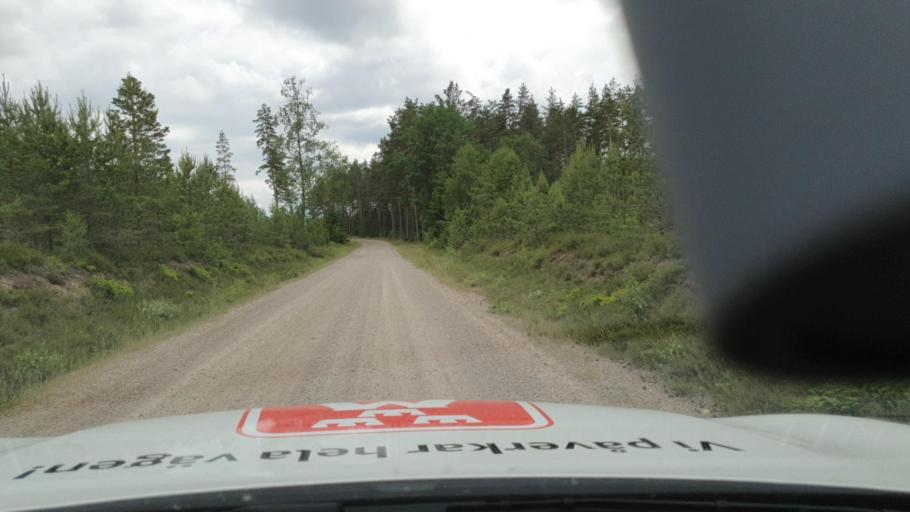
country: SE
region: Vaestra Goetaland
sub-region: Tidaholms Kommun
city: Olofstorp
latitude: 58.1979
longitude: 14.1089
